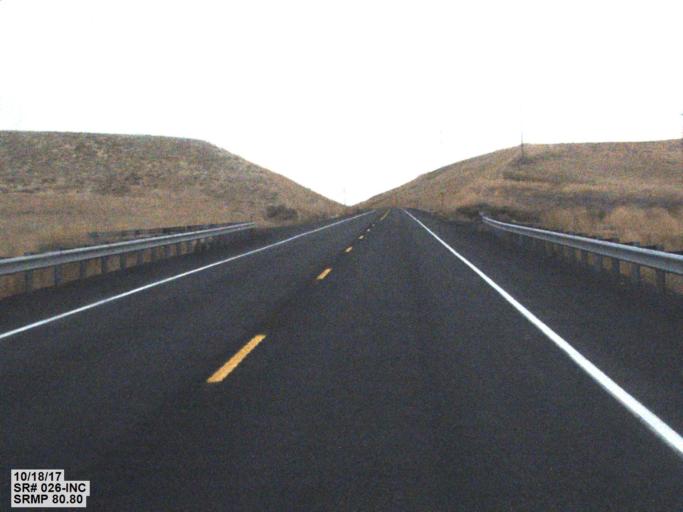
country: US
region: Washington
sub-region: Adams County
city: Ritzville
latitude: 46.7694
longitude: -118.3500
